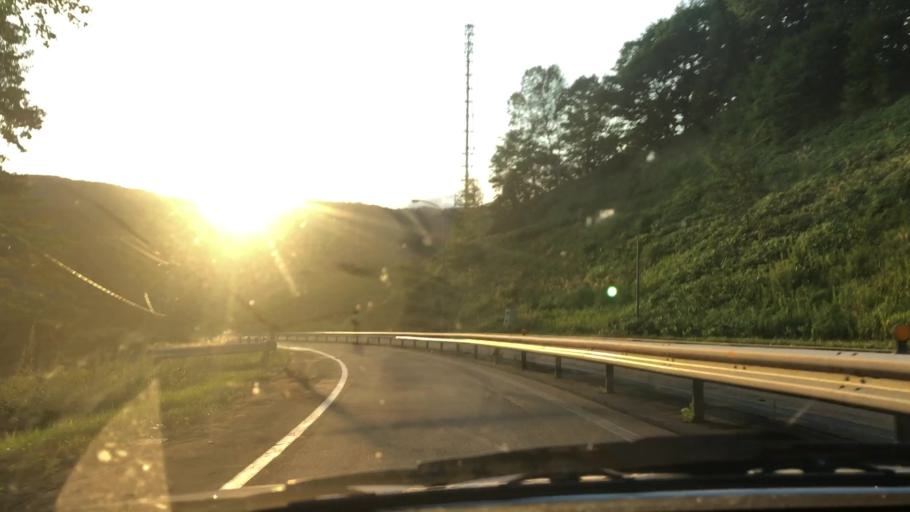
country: JP
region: Hokkaido
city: Shimo-furano
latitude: 42.8869
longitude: 142.2613
